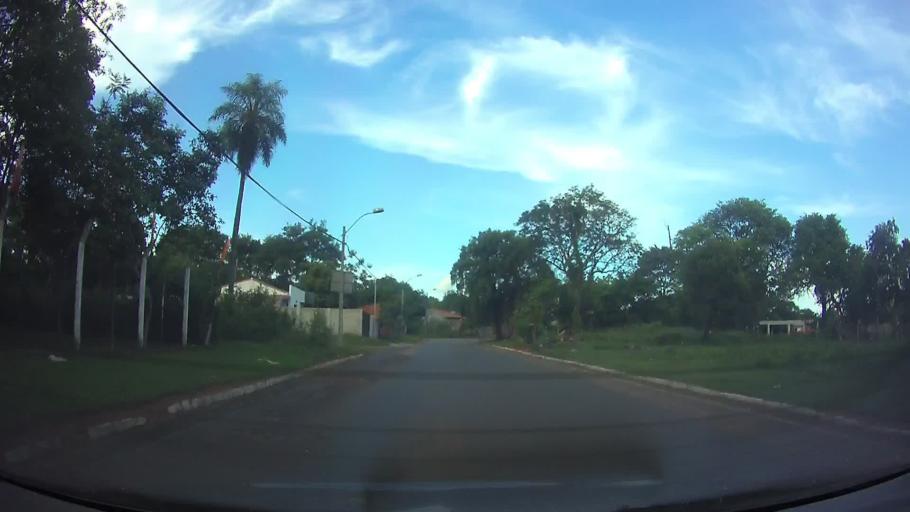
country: PY
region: Central
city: San Antonio
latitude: -25.4273
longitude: -57.5463
